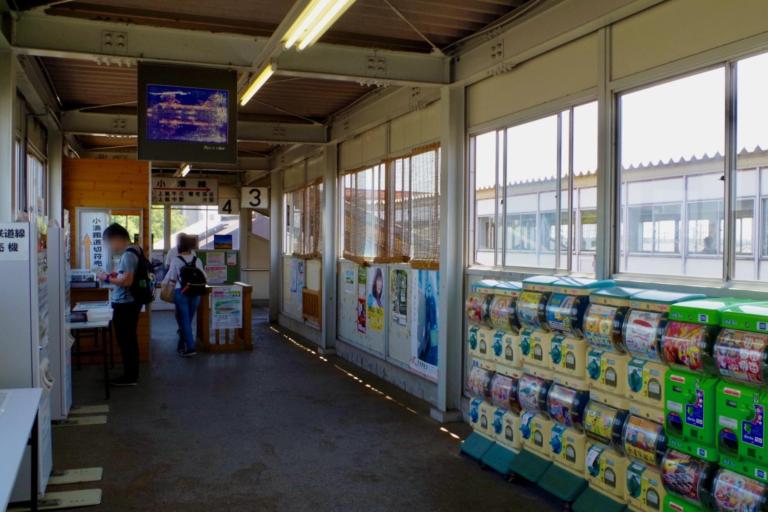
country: JP
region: Chiba
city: Ichihara
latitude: 35.5132
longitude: 140.0899
